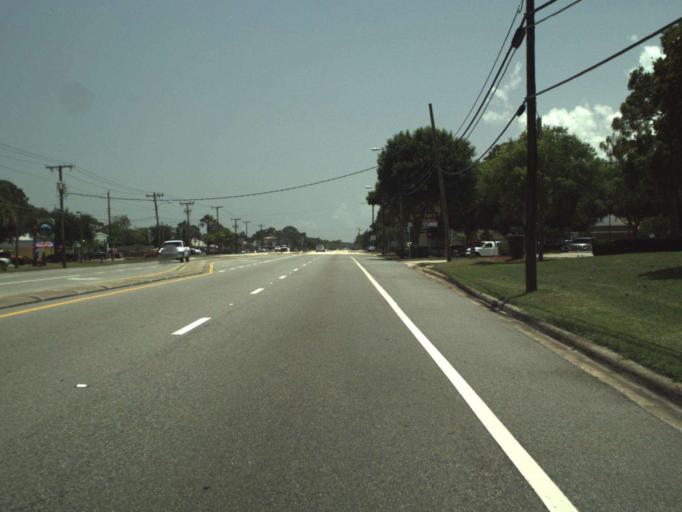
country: US
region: Florida
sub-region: Volusia County
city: Edgewater
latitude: 28.9812
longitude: -80.9014
